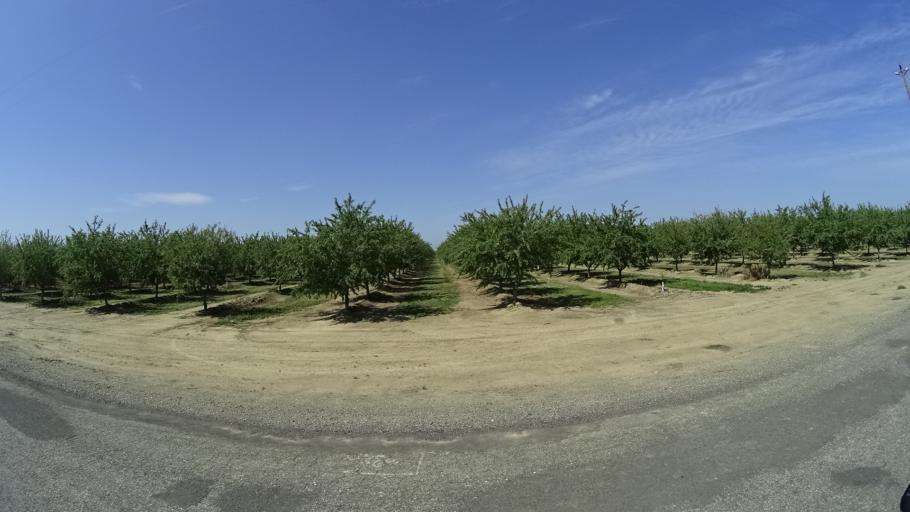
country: US
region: California
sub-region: Glenn County
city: Hamilton City
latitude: 39.6476
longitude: -122.0743
